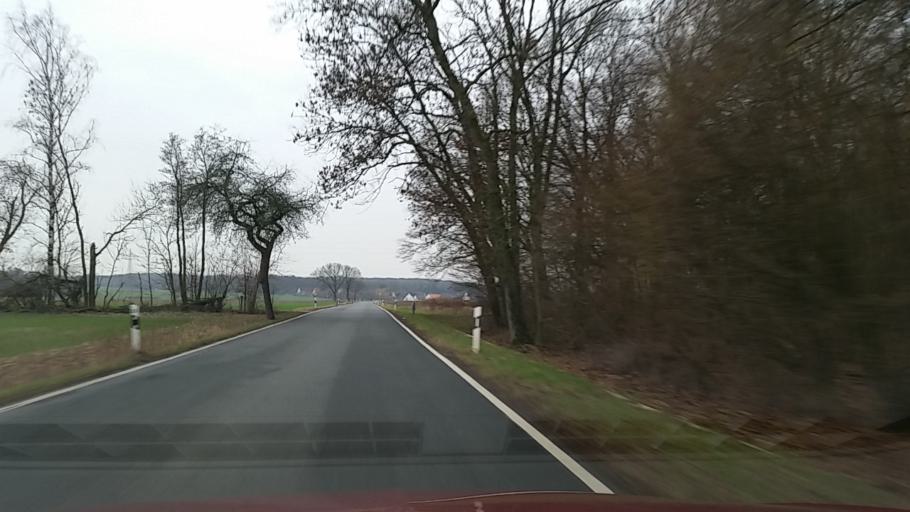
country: DE
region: Lower Saxony
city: Meine
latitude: 52.3476
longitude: 10.5859
